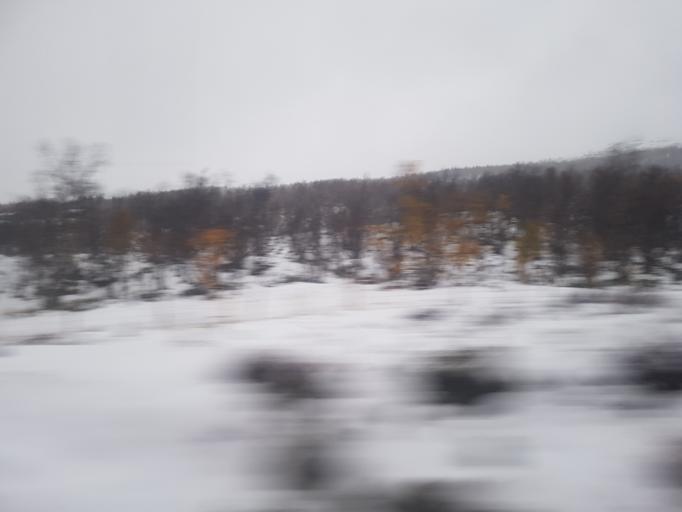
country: NO
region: Oppland
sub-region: Dovre
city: Dovre
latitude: 62.1730
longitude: 9.4447
